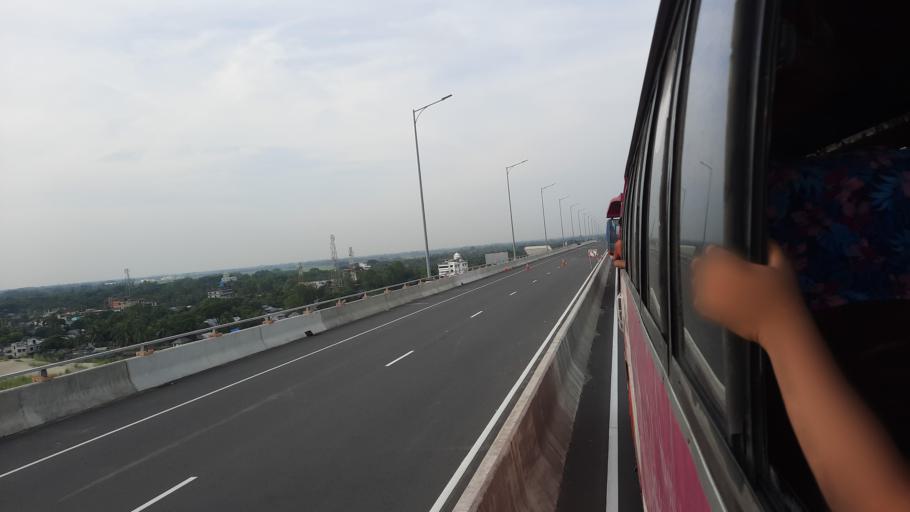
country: BD
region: Dhaka
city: Char Bhadrasan
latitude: 23.4688
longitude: 90.2640
